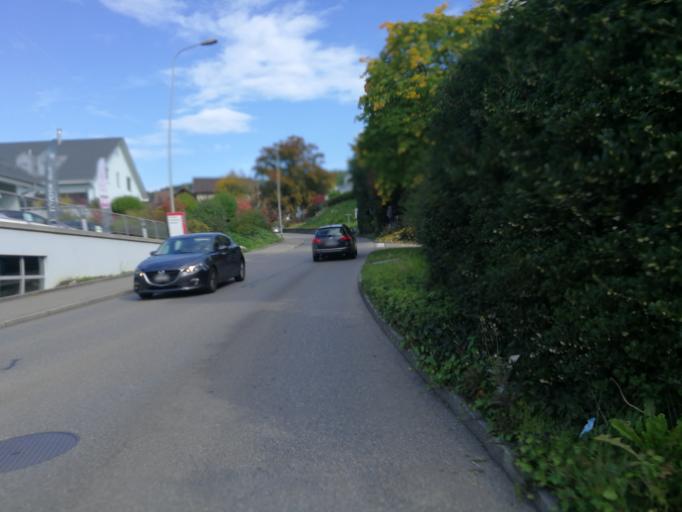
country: CH
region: Zurich
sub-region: Bezirk Meilen
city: Mannedorf
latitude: 47.2573
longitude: 8.7038
